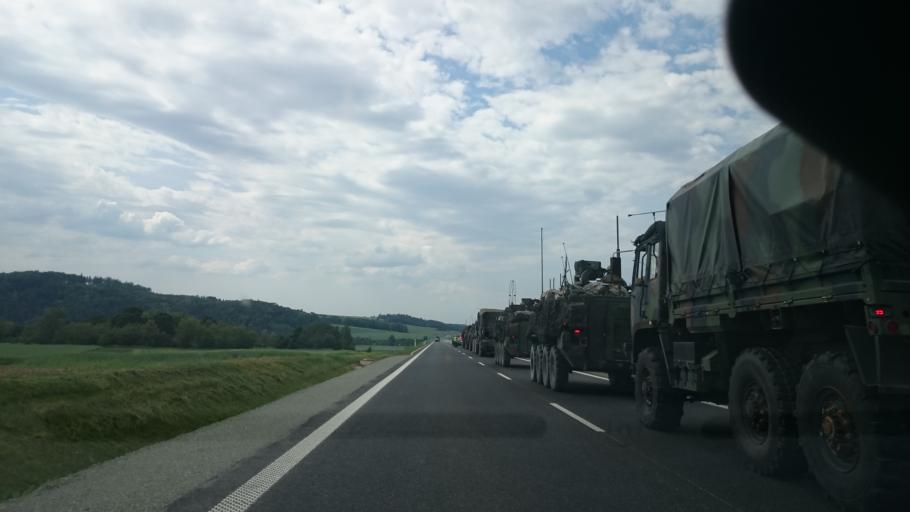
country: PL
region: Lower Silesian Voivodeship
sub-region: Powiat klodzki
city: Klodzko
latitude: 50.4010
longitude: 16.6485
